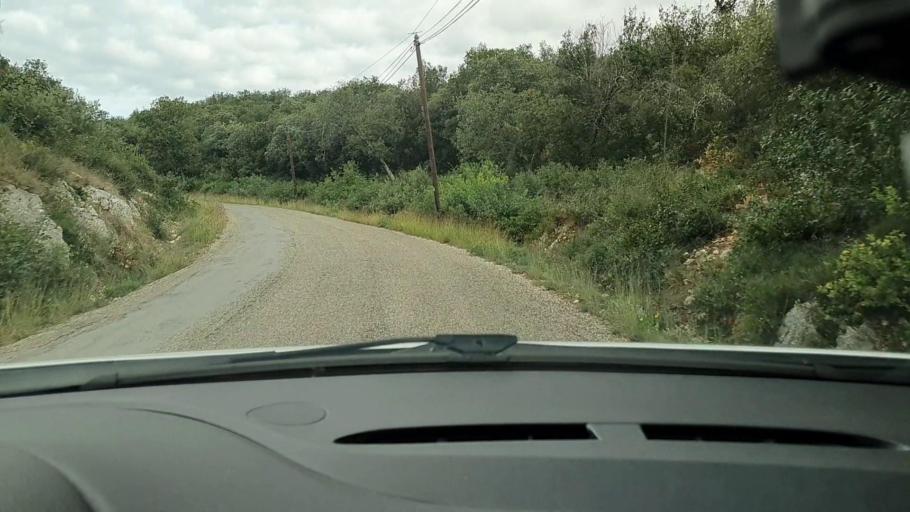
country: FR
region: Languedoc-Roussillon
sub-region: Departement du Gard
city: Montaren-et-Saint-Mediers
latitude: 44.0622
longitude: 4.3164
